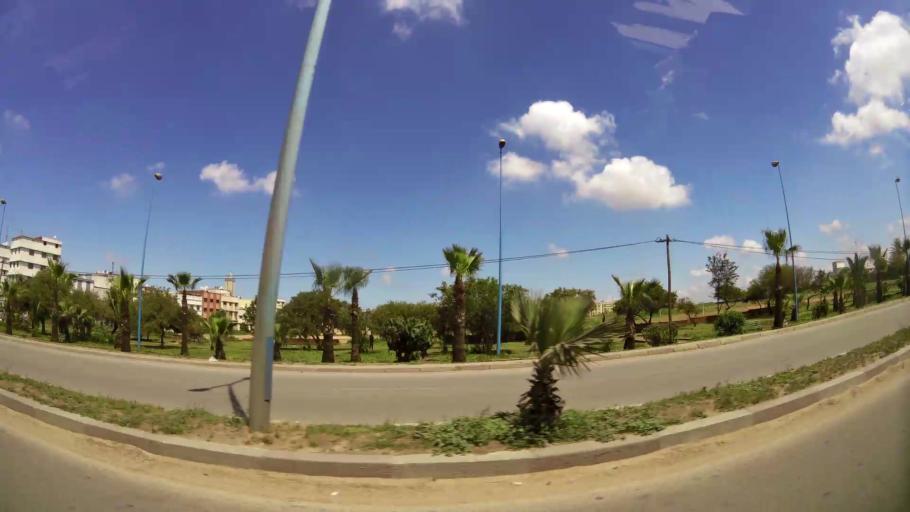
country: MA
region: Grand Casablanca
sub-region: Casablanca
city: Casablanca
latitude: 33.5342
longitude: -7.5731
